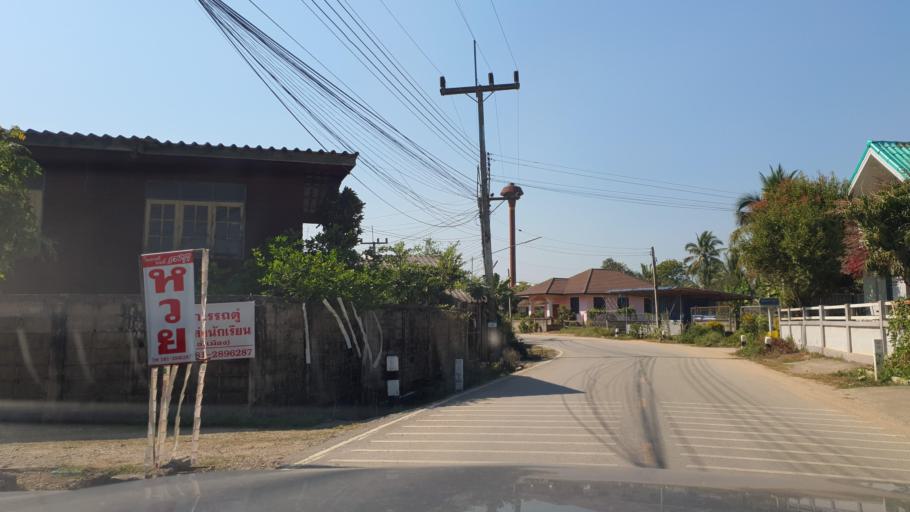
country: TH
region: Chiang Rai
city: Mae Lao
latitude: 19.7643
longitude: 99.7278
